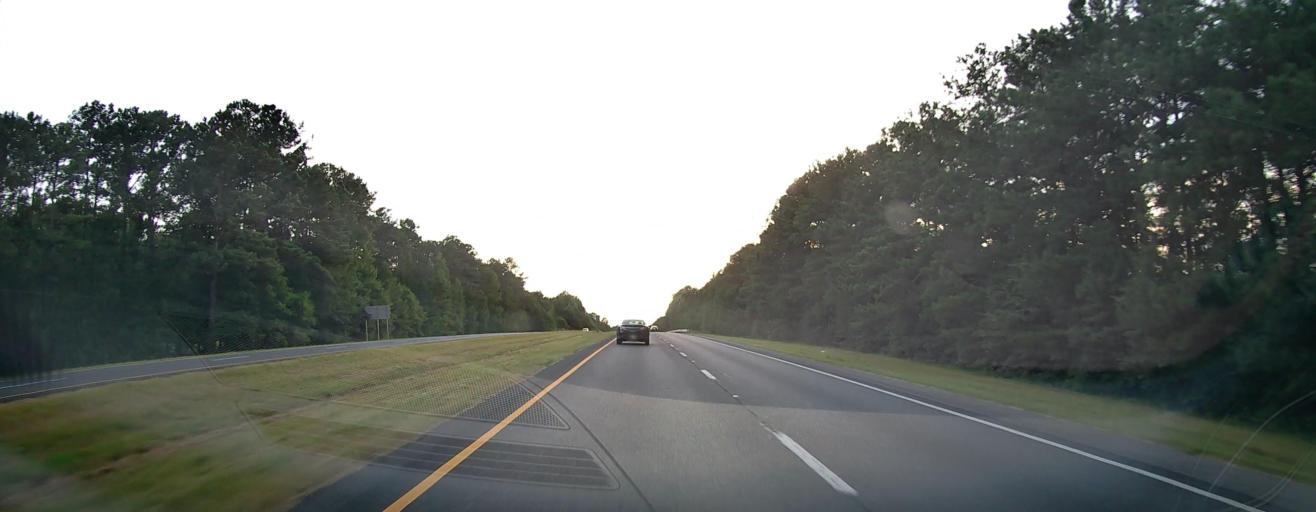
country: US
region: Georgia
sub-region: Muscogee County
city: Columbus
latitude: 32.5207
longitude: -84.9023
